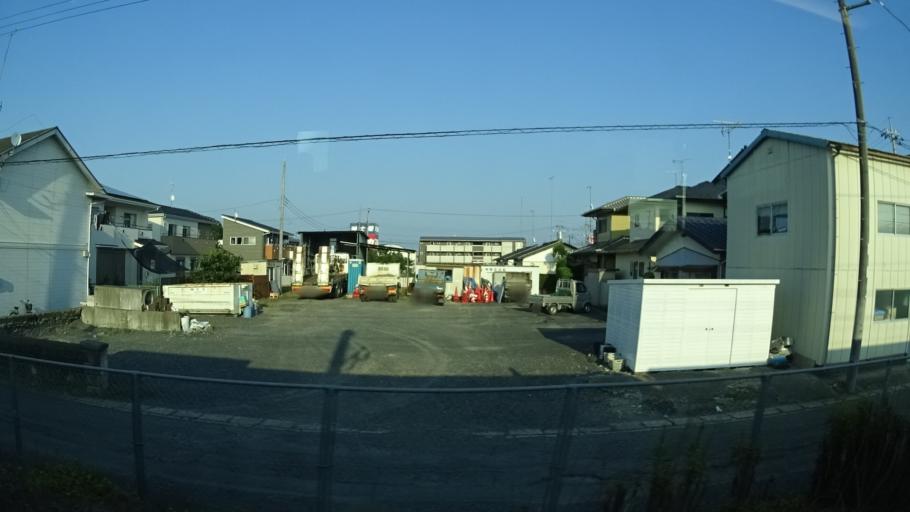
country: JP
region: Ibaraki
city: Hitachi-Naka
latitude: 36.4055
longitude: 140.5285
